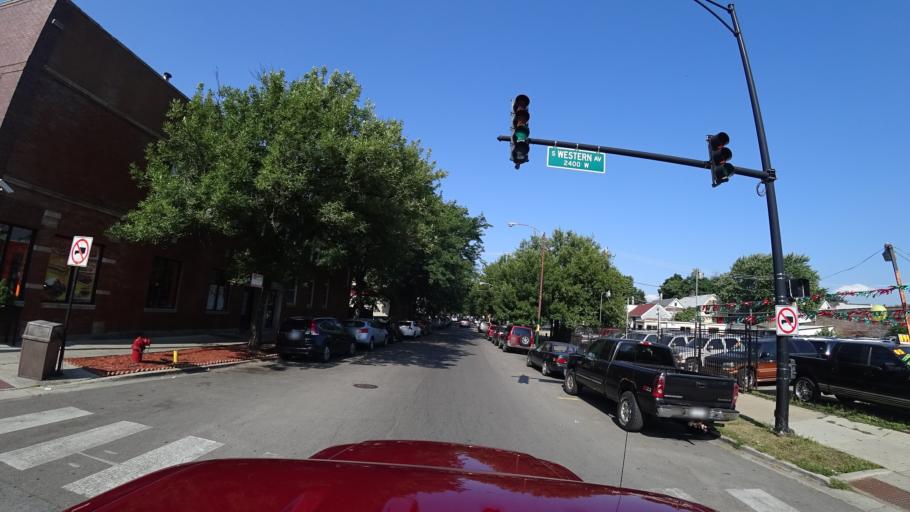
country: US
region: Illinois
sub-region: Cook County
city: Chicago
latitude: 41.8157
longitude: -87.6847
